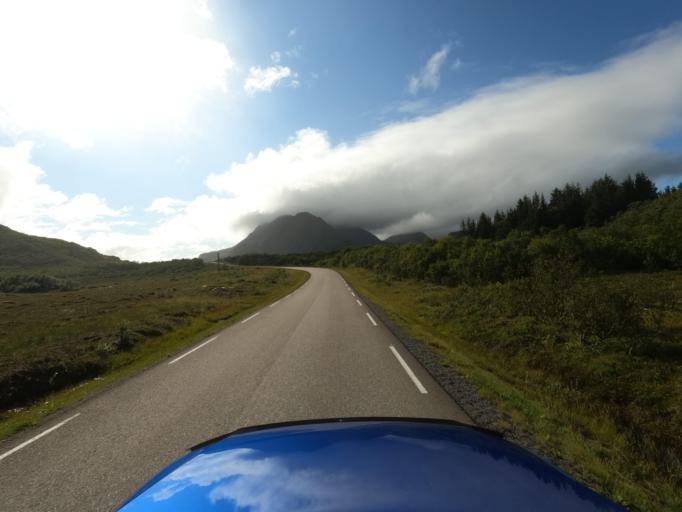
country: NO
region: Nordland
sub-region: Vagan
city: Kabelvag
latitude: 68.2849
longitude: 14.1598
